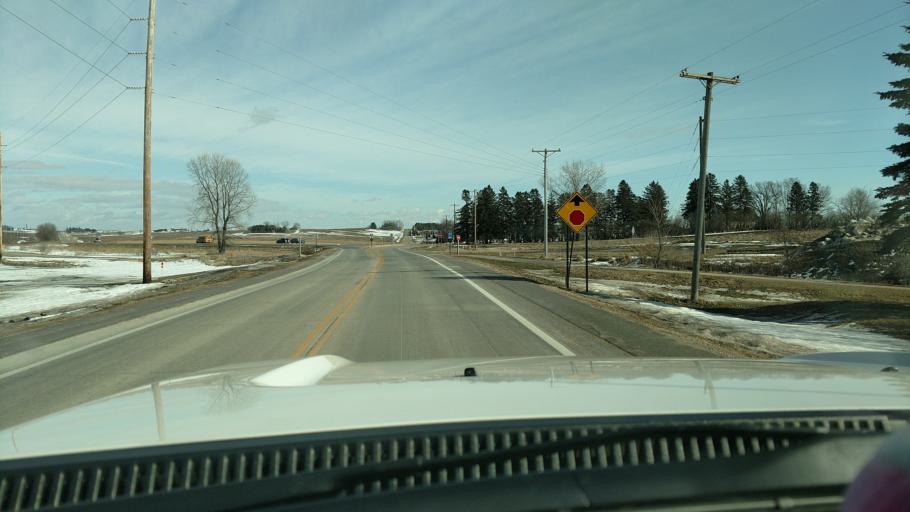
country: US
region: Minnesota
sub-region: Wabasha County
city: Elgin
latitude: 44.1364
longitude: -92.2500
